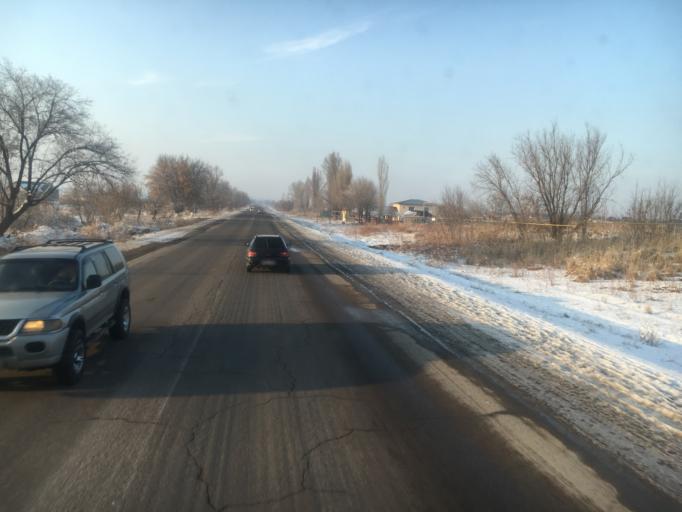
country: KZ
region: Almaty Oblysy
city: Burunday
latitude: 43.3419
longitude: 76.6577
